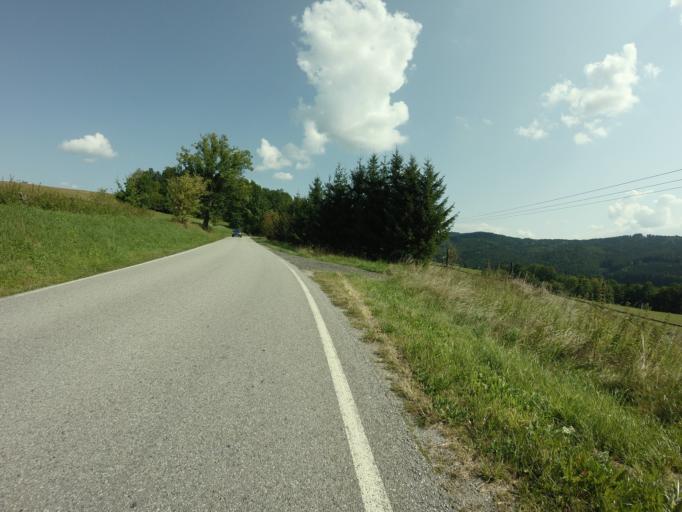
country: CZ
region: Jihocesky
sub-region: Okres Cesky Krumlov
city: Vyssi Brod
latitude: 48.6440
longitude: 14.3578
